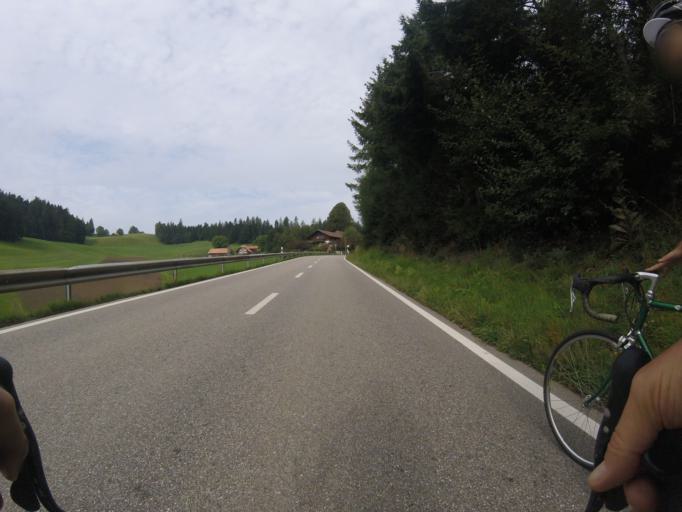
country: CH
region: Bern
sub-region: Bern-Mittelland District
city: Walkringen
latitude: 46.9466
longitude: 7.6490
